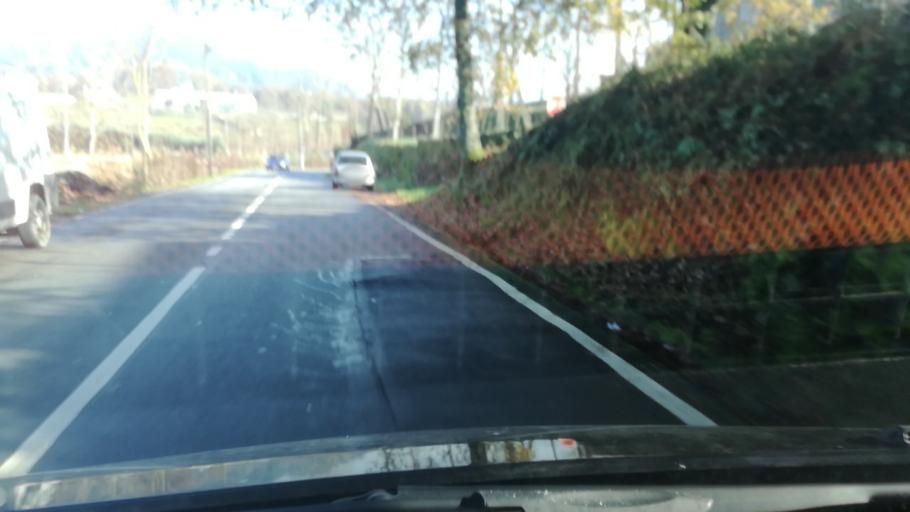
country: PT
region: Braga
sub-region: Guimaraes
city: Ponte
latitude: 41.5168
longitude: -8.3323
